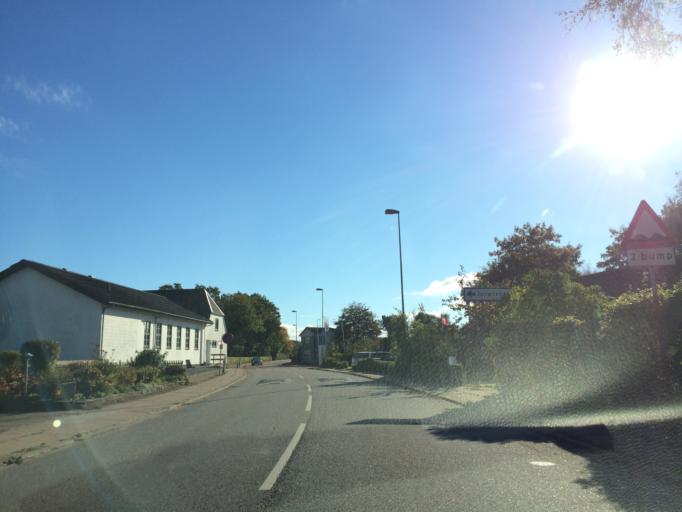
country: DK
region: Central Jutland
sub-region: Randers Kommune
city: Langa
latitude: 56.3569
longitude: 9.9162
